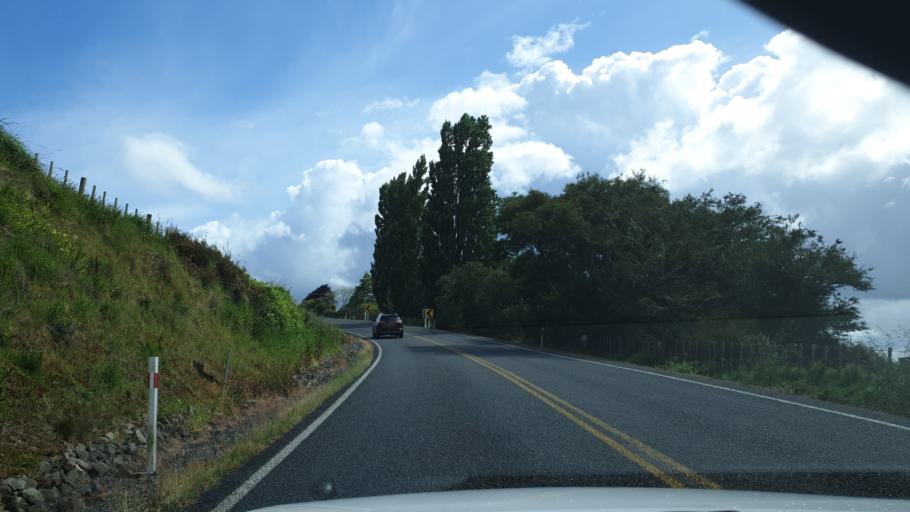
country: NZ
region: Waikato
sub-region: Matamata-Piako District
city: Matamata
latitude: -37.8727
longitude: 175.6861
